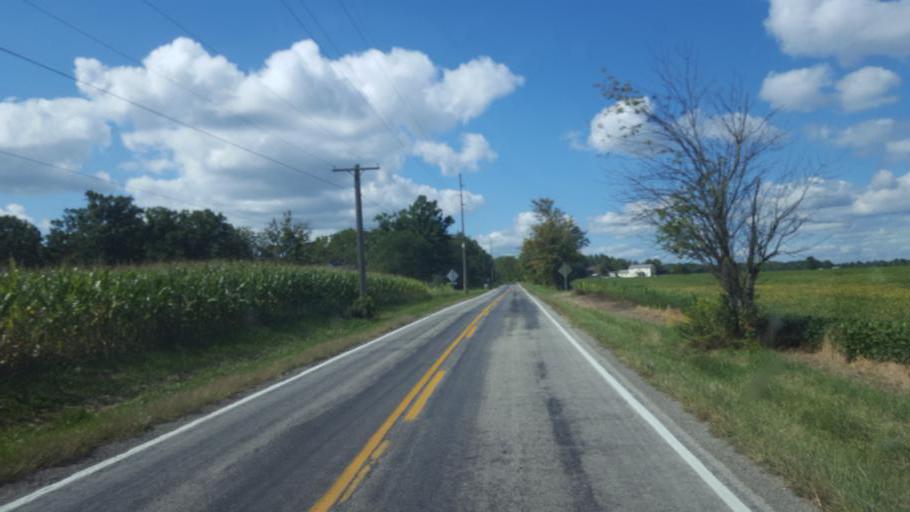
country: US
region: Ohio
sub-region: Lorain County
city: Lagrange
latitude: 41.1914
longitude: -82.1025
